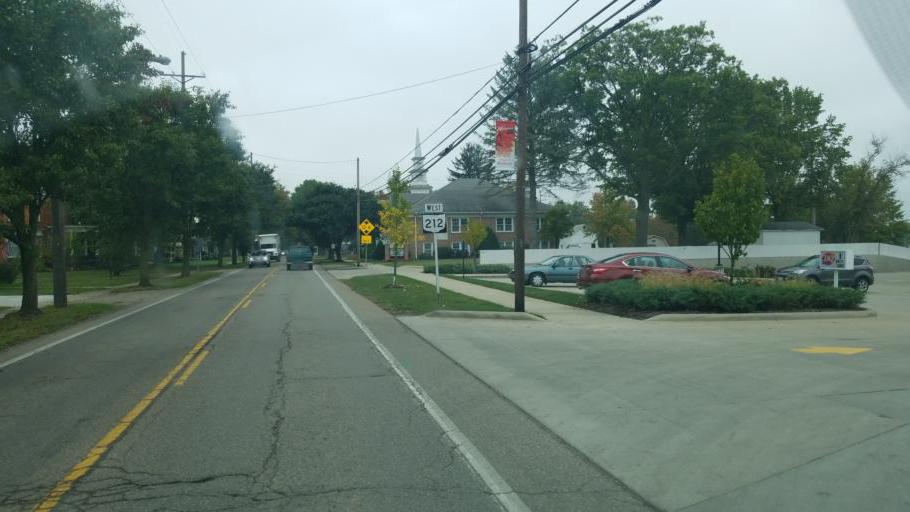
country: US
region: Ohio
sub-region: Tuscarawas County
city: Strasburg
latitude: 40.6451
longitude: -81.4544
